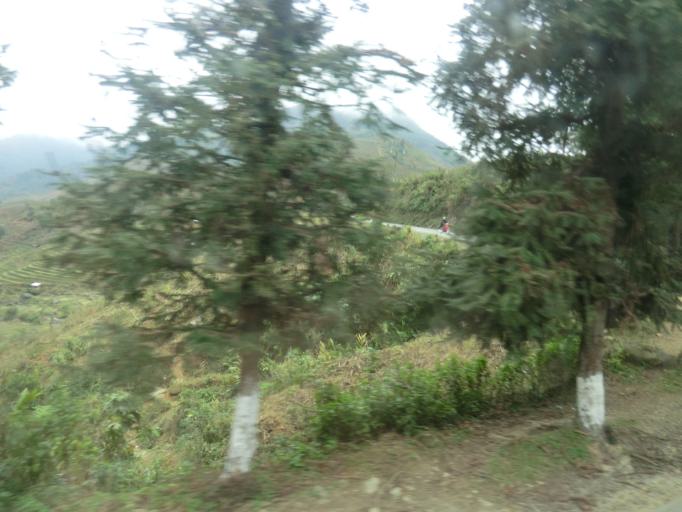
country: VN
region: Lao Cai
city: Sa Pa
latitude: 22.4115
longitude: 103.8995
